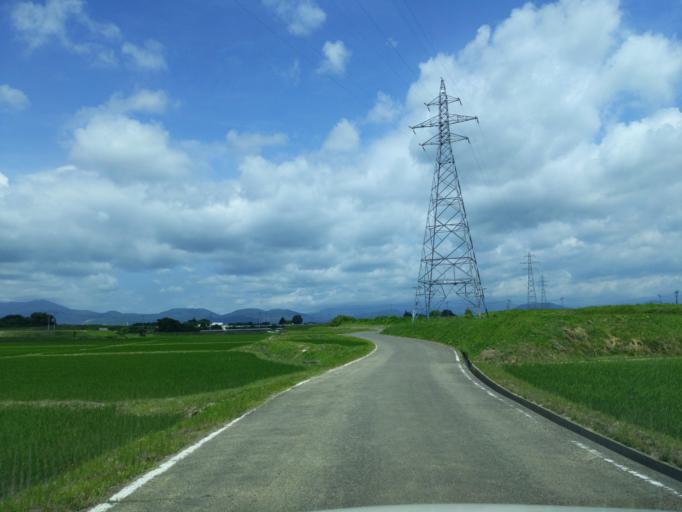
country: JP
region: Fukushima
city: Koriyama
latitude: 37.4384
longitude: 140.3583
